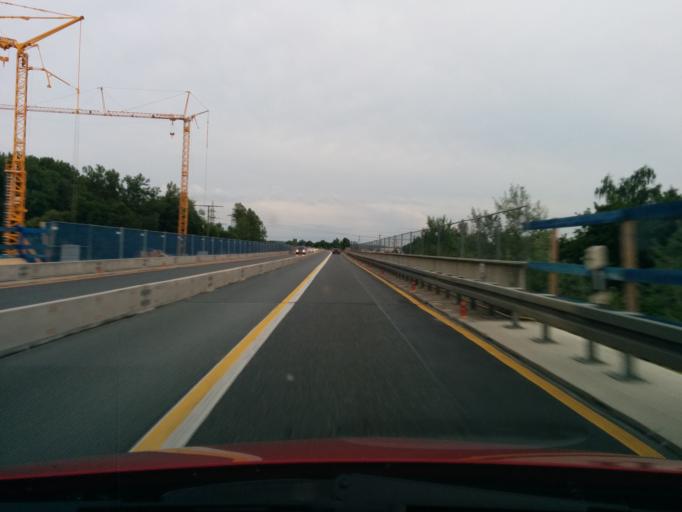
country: DE
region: Bavaria
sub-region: Upper Franconia
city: Forchheim
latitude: 49.7150
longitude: 11.0524
